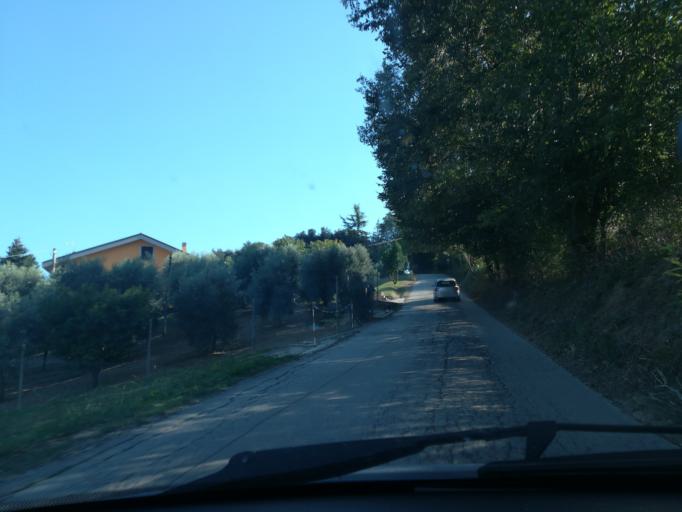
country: IT
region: The Marches
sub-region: Provincia di Macerata
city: Macerata
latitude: 43.3047
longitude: 13.4783
